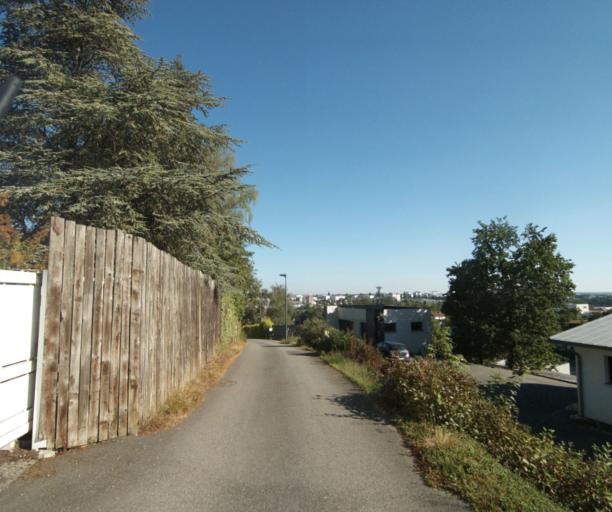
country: FR
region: Lorraine
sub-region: Departement des Vosges
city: Epinal
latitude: 48.1707
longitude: 6.4575
